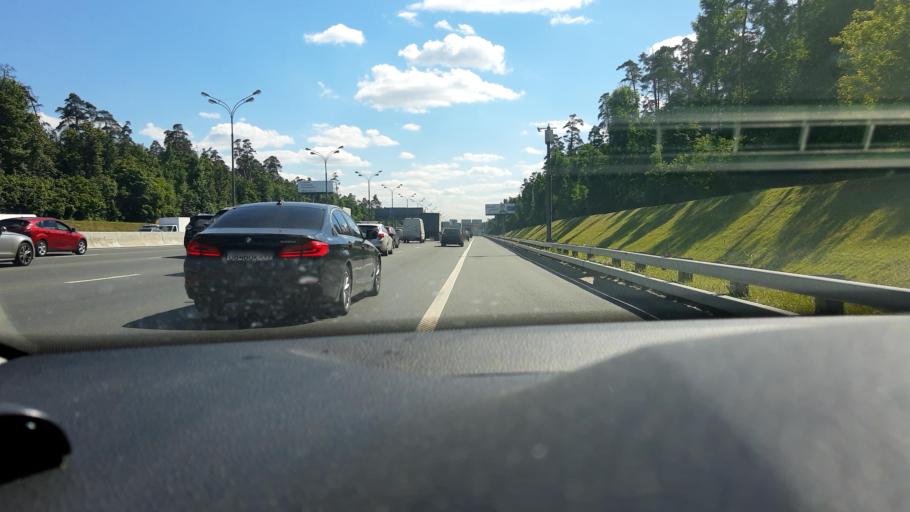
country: RU
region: Moscow
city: Rublevo
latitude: 55.7820
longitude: 37.3691
